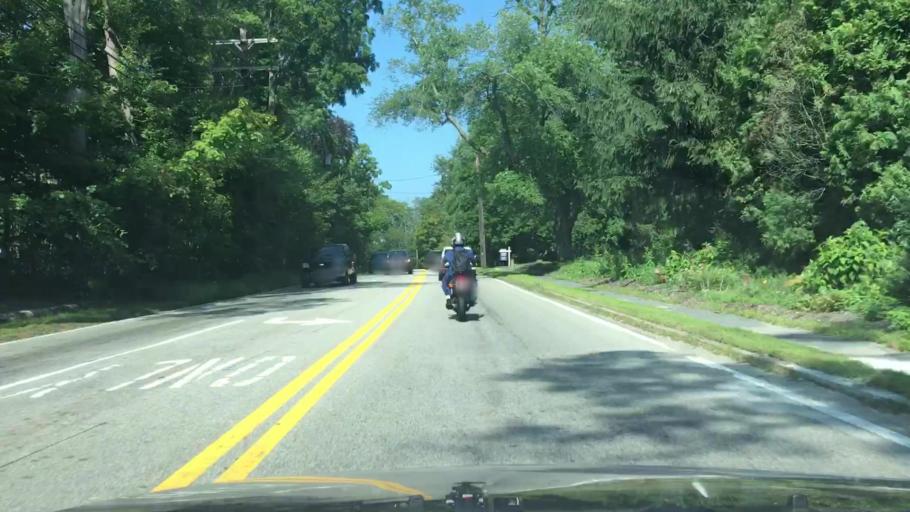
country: US
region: Massachusetts
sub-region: Middlesex County
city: Holliston
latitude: 42.1912
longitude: -71.4371
